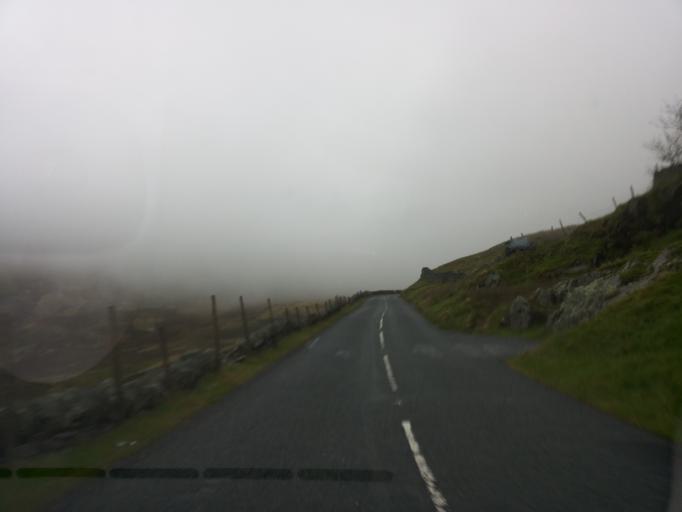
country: GB
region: England
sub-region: Cumbria
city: Ambleside
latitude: 54.4609
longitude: -2.9265
